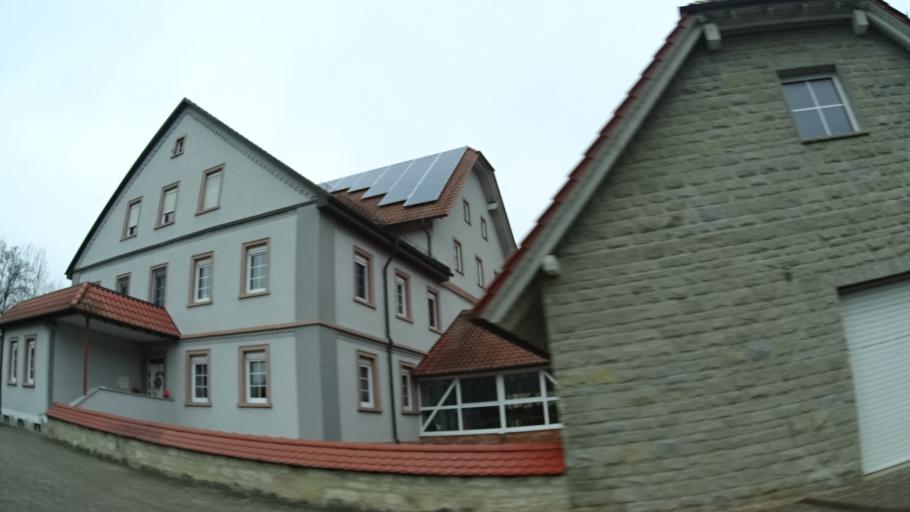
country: DE
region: Baden-Wuerttemberg
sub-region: Regierungsbezirk Stuttgart
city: Lauda-Konigshofen
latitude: 49.5199
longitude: 9.7043
